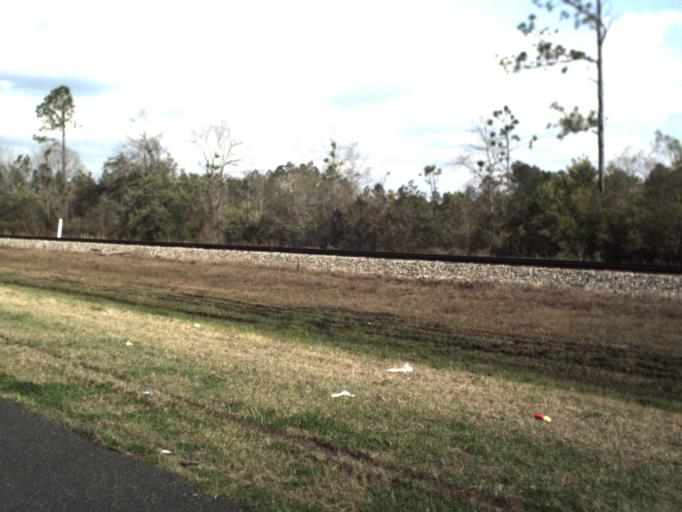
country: US
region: Florida
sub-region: Bay County
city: Youngstown
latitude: 30.2845
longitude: -85.5065
